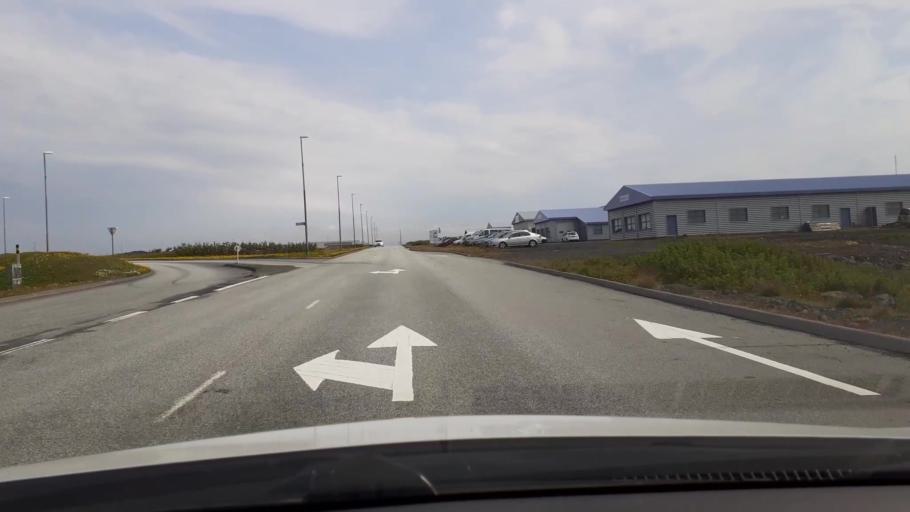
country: IS
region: Southern Peninsula
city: Reykjanesbaer
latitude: 63.9721
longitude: -22.5302
